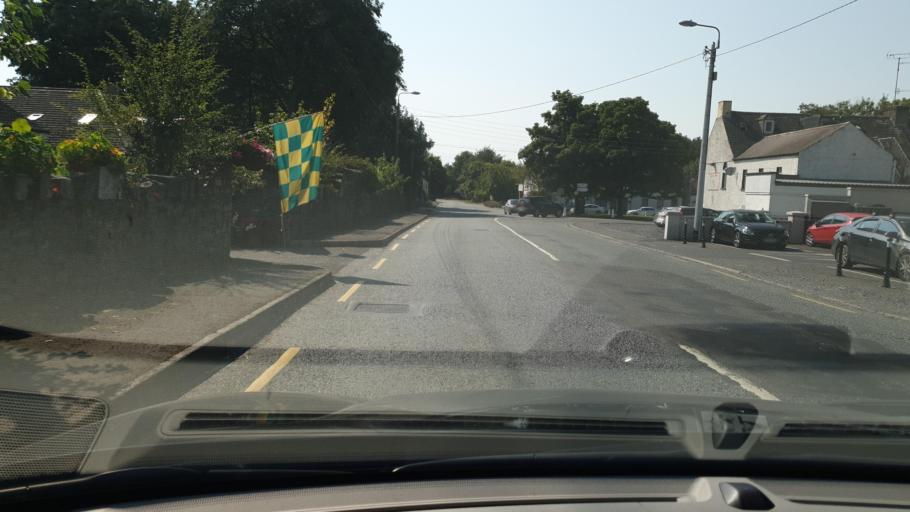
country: IE
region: Leinster
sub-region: An Mhi
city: Newtown Trim
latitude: 53.4803
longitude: -6.7307
